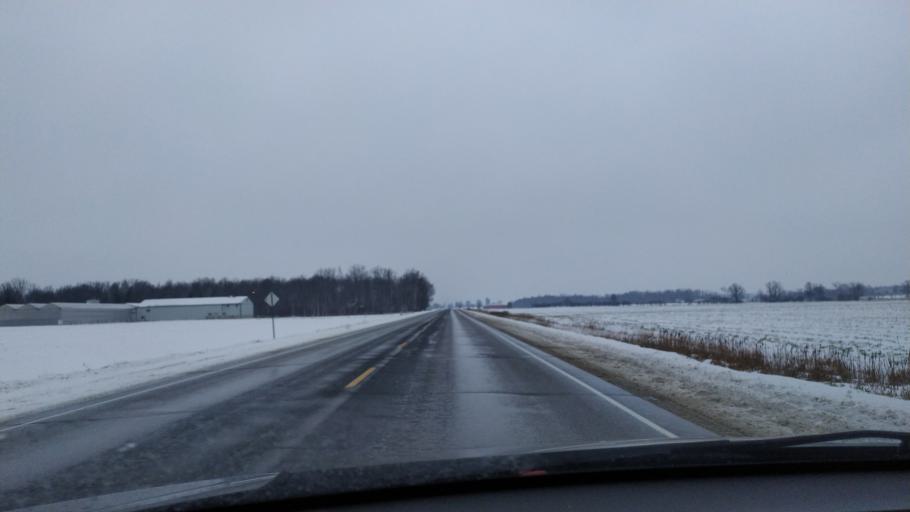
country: CA
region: Ontario
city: North Perth
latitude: 43.5852
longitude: -80.8293
